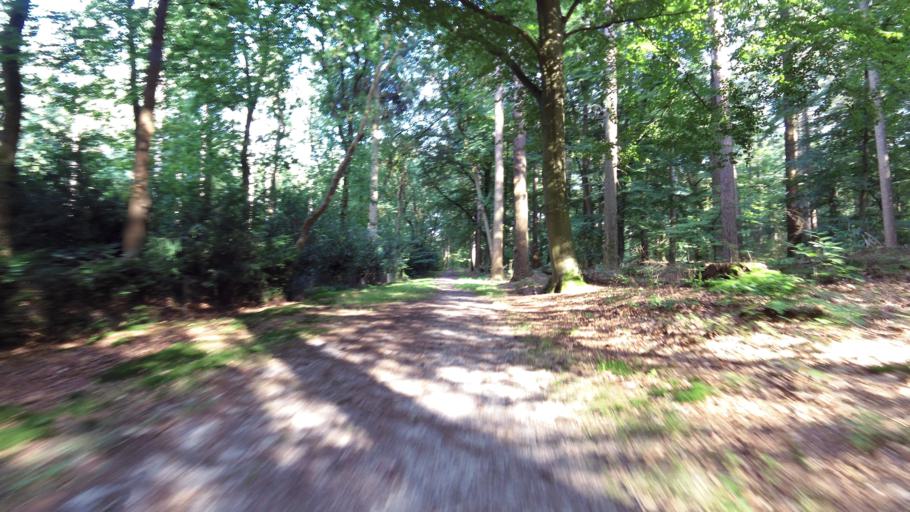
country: NL
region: Utrecht
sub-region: Gemeente Soest
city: Soest
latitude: 52.1361
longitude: 5.2862
